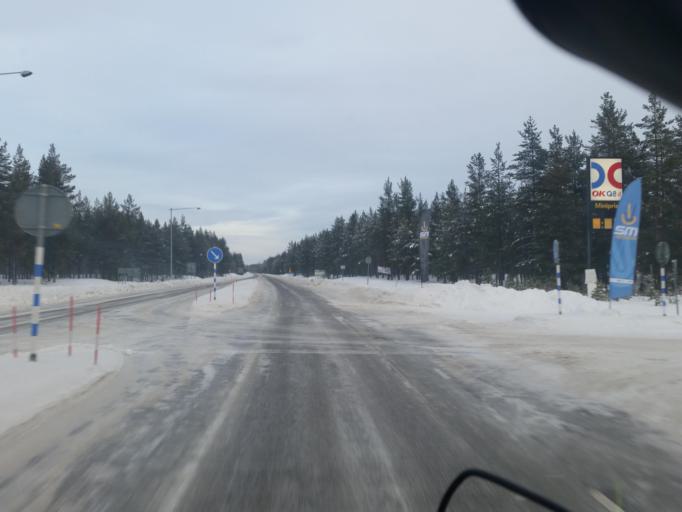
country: SE
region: Norrbotten
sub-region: Pitea Kommun
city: Pitea
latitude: 65.2366
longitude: 21.5257
